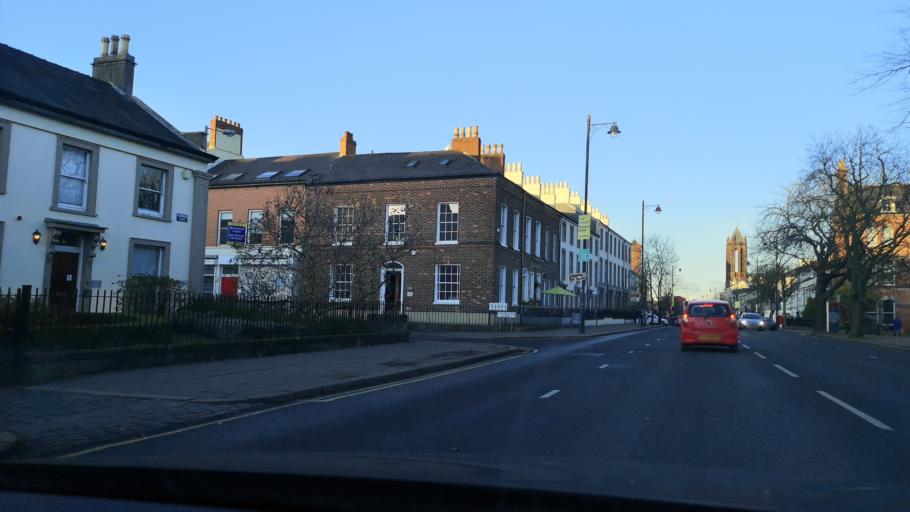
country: GB
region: Northern Ireland
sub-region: City of Belfast
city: Belfast
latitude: 54.5849
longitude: -5.9363
